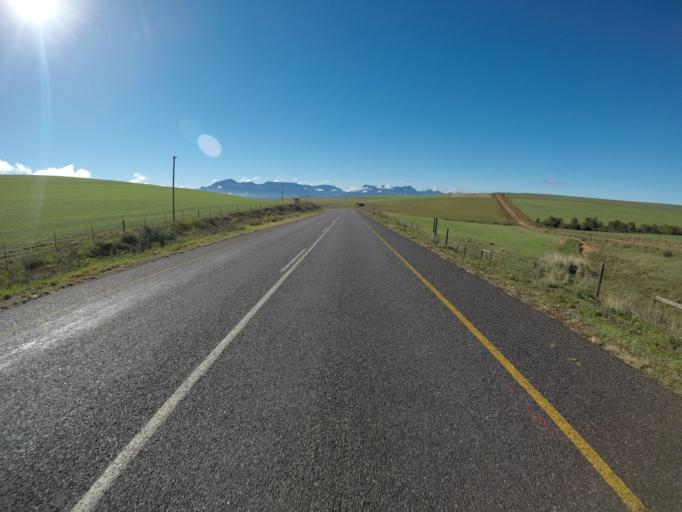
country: ZA
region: Western Cape
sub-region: Overberg District Municipality
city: Caledon
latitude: -34.1388
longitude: 19.5054
